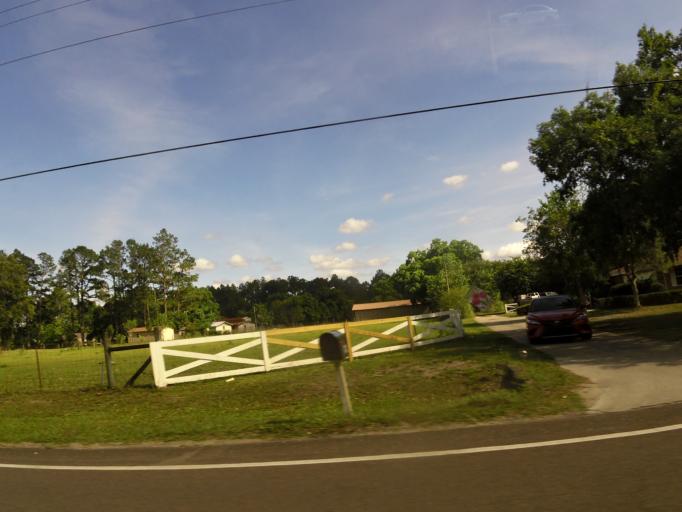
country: US
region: Florida
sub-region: Nassau County
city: Callahan
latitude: 30.5582
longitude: -81.8651
